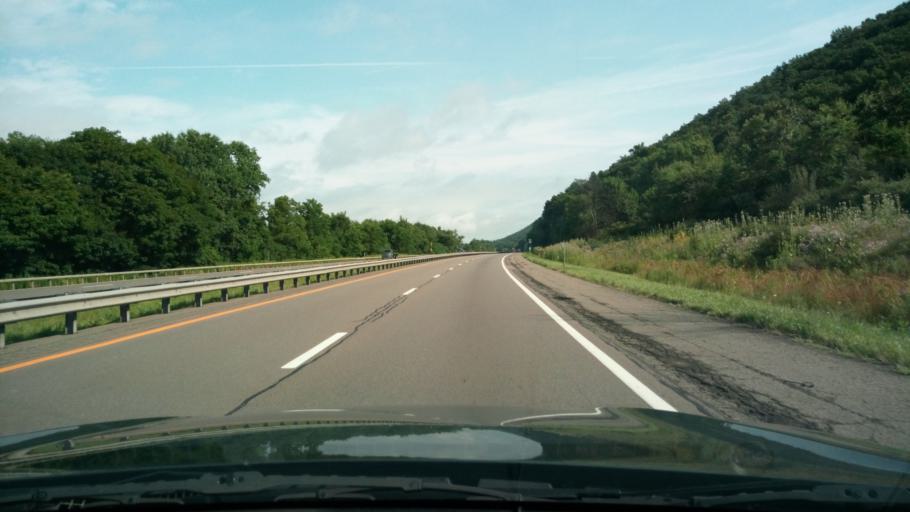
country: US
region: New York
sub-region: Chemung County
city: Elmira Heights
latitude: 42.1219
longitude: -76.8017
